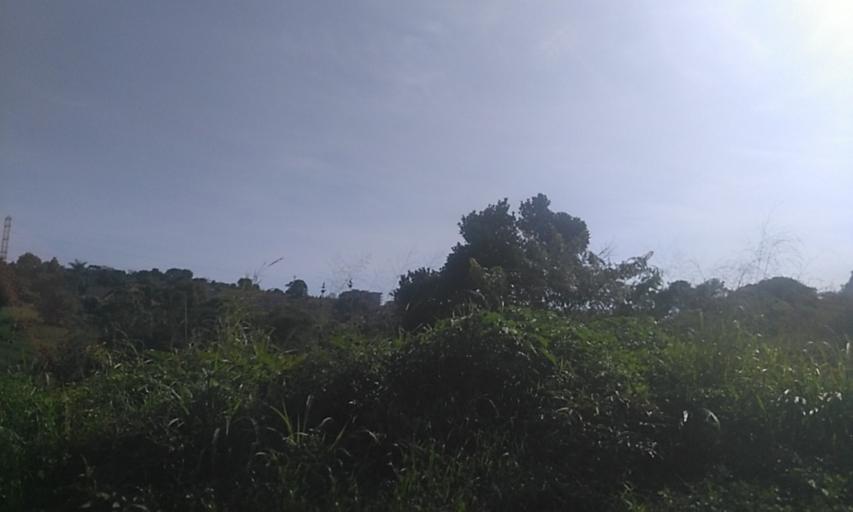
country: UG
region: Central Region
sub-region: Wakiso District
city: Kireka
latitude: 0.3637
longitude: 32.6310
